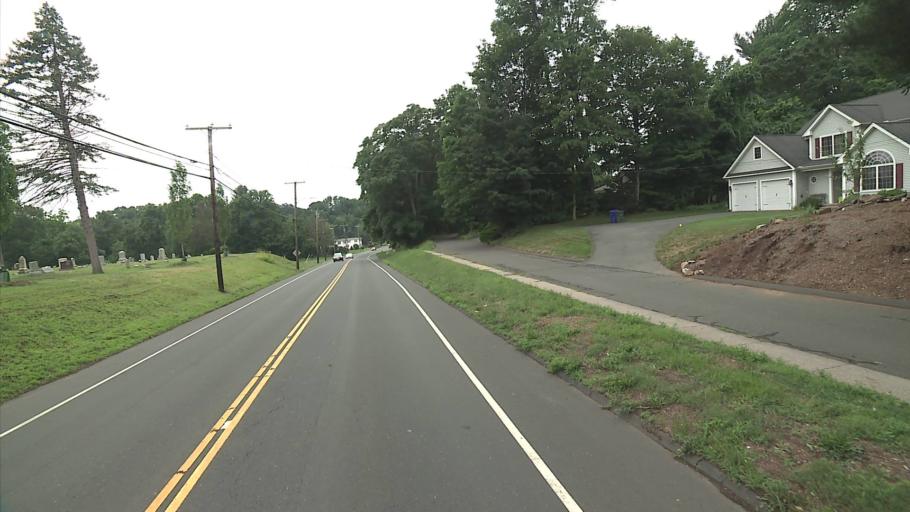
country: US
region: Connecticut
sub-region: Hartford County
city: Wethersfield
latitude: 41.6601
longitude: -72.6393
